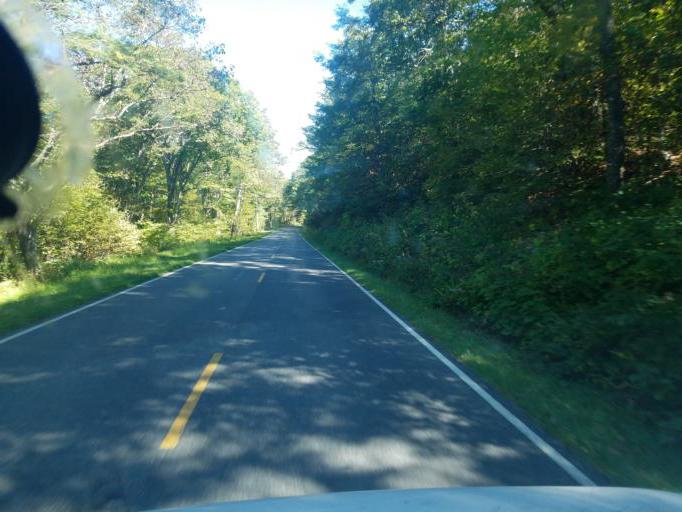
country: US
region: Virginia
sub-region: Rockingham County
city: Elkton
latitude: 38.3762
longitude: -78.5267
